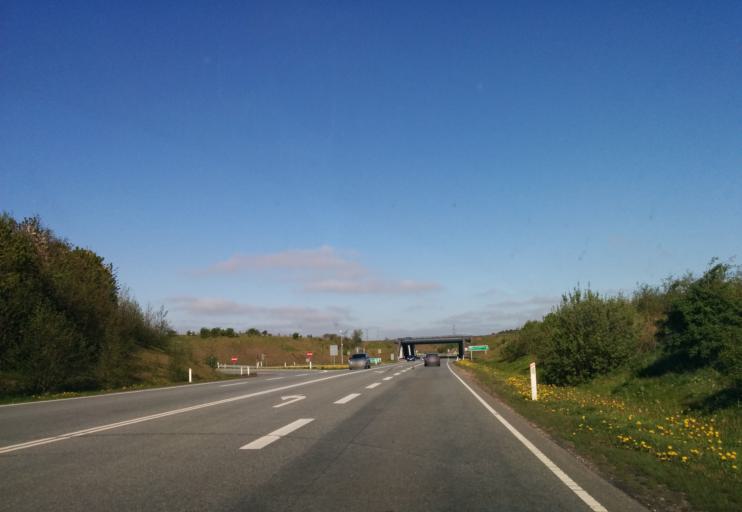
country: DK
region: Central Jutland
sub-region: Arhus Kommune
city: Kolt
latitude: 56.1195
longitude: 10.0859
